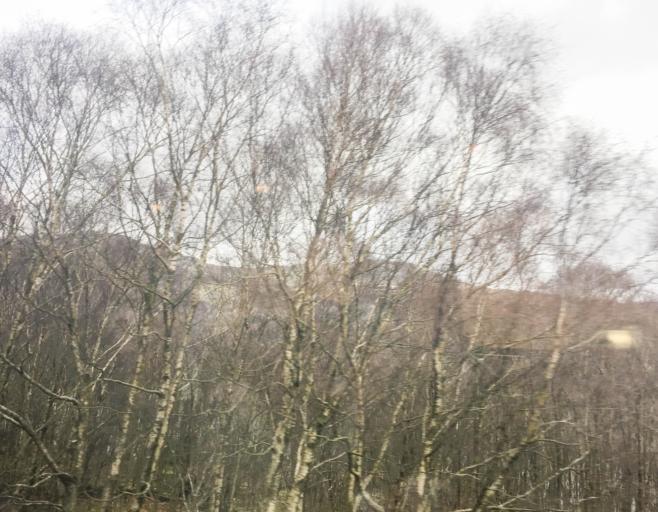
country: GB
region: Scotland
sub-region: Argyll and Bute
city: Garelochhead
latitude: 56.2541
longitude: -4.7101
